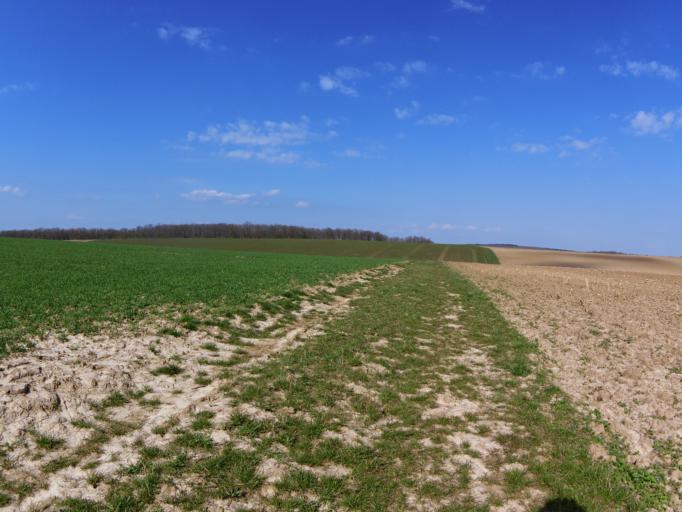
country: DE
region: Bavaria
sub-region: Regierungsbezirk Unterfranken
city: Rottendorf
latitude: 49.7975
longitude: 10.0605
